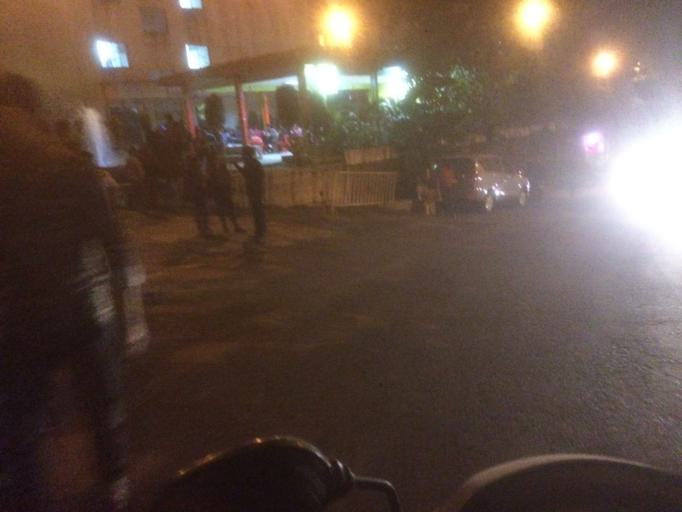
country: IN
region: Maharashtra
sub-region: Pune Division
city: Pune
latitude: 18.4650
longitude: 73.8368
